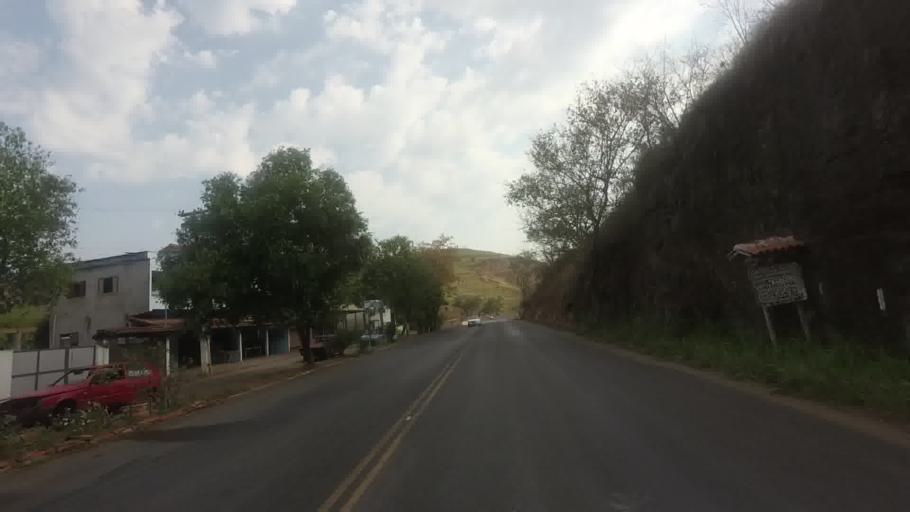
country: BR
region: Rio de Janeiro
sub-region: Itaperuna
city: Itaperuna
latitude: -21.3608
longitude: -41.9256
